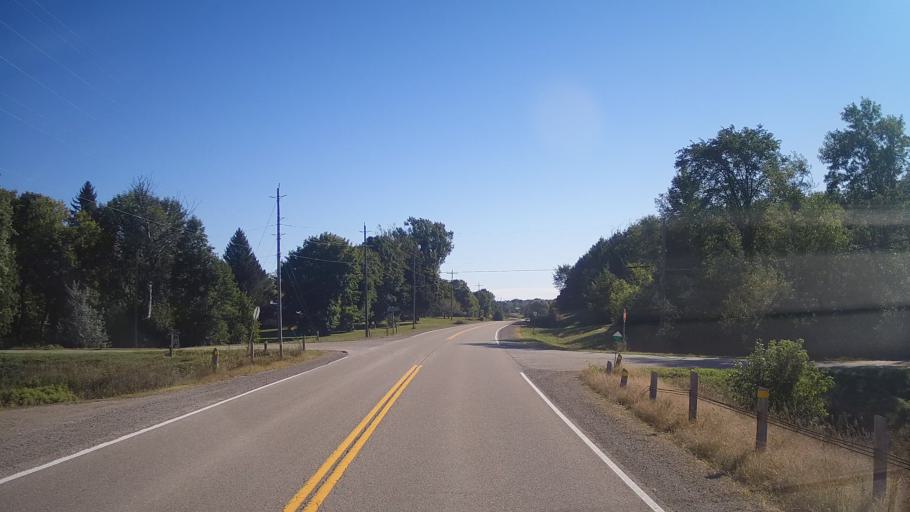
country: CA
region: Ontario
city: Gananoque
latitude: 44.6076
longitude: -76.0697
